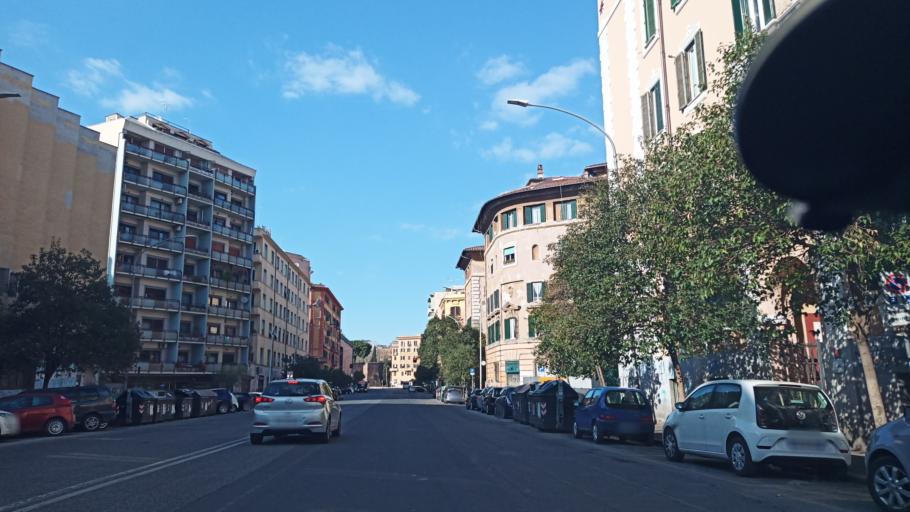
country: IT
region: Latium
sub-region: Citta metropolitana di Roma Capitale
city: Rome
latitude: 41.8828
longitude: 12.5086
